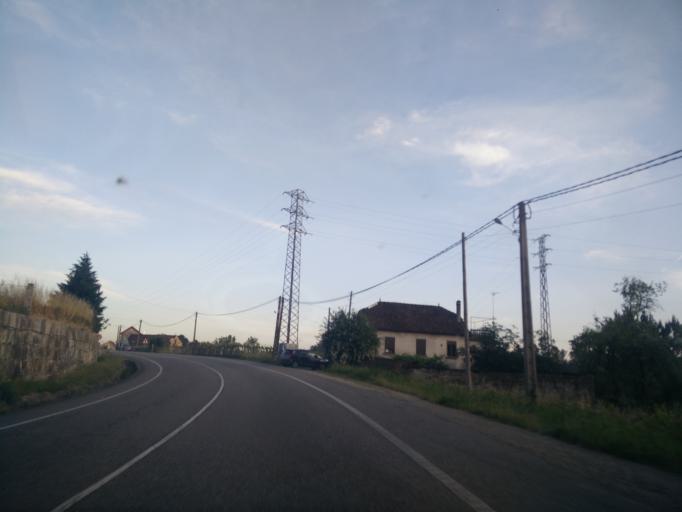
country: ES
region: Galicia
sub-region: Provincia de Pontevedra
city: Ponteareas
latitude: 42.1896
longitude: -8.5084
